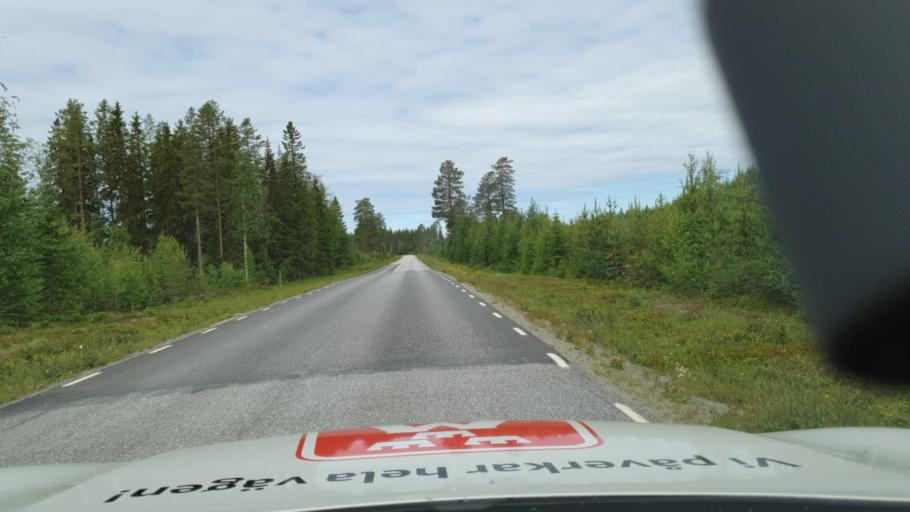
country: SE
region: Vaesterbotten
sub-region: Skelleftea Kommun
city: Langsele
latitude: 64.5369
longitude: 20.2894
